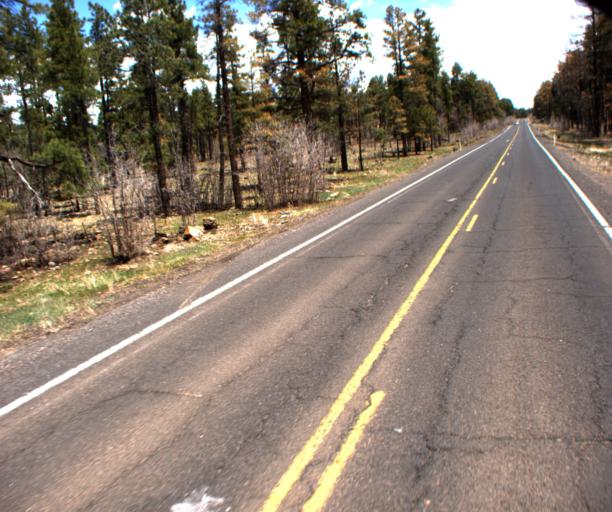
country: US
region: Arizona
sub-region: Coconino County
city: Kachina Village
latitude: 35.1016
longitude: -111.7296
